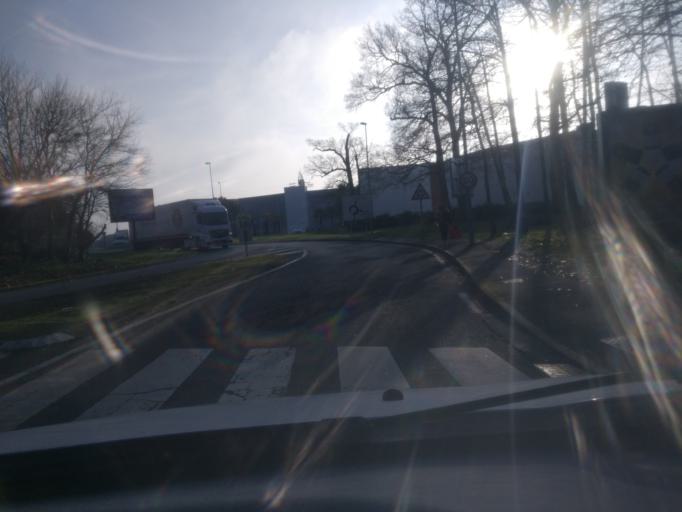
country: FR
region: Pays de la Loire
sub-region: Departement de la Loire-Atlantique
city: Vertou
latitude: 47.1892
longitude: -1.4719
